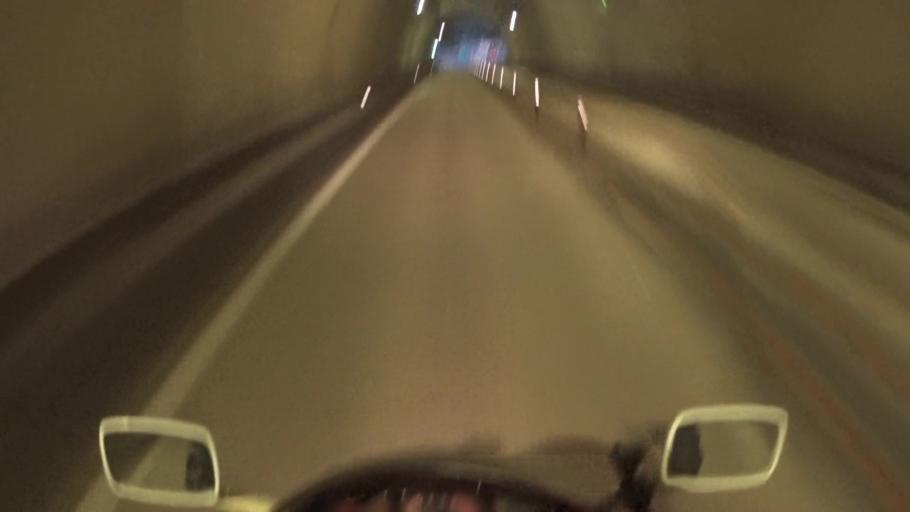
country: JP
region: Kyoto
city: Miyazu
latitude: 35.5443
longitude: 135.1540
